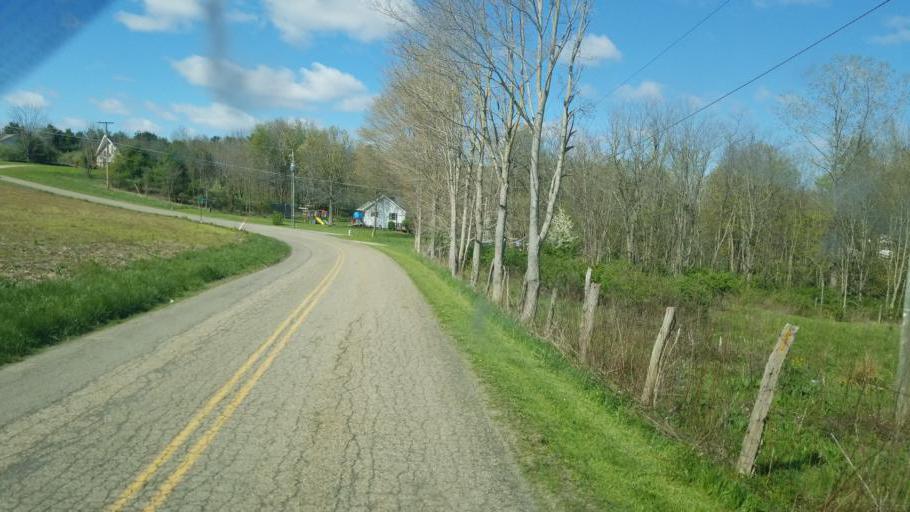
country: US
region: Ohio
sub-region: Knox County
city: Danville
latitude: 40.4327
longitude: -82.3360
